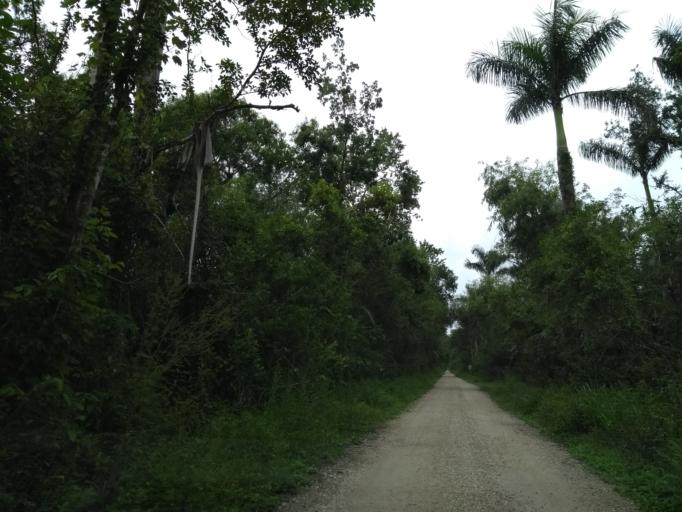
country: US
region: Florida
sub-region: Collier County
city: Lely Resort
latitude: 26.0065
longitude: -81.4112
